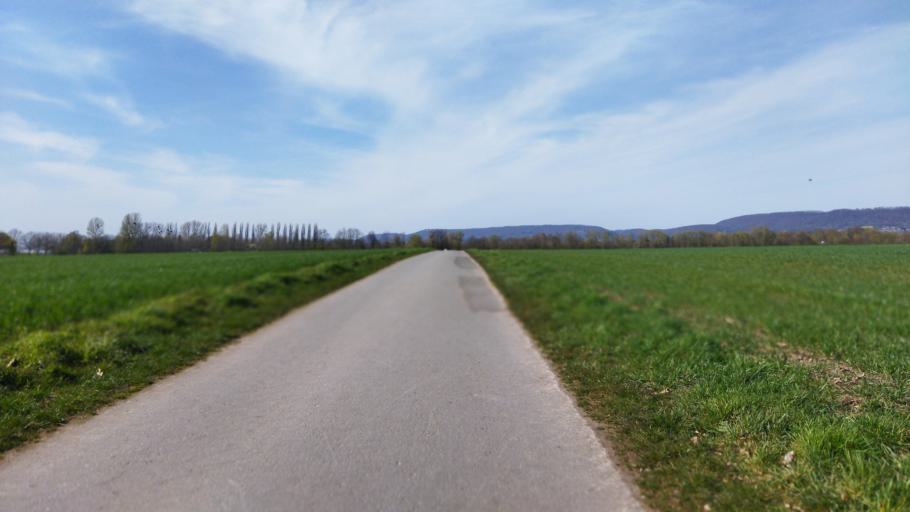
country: DE
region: Lower Saxony
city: Hessisch Oldendorf
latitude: 52.1432
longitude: 9.2844
